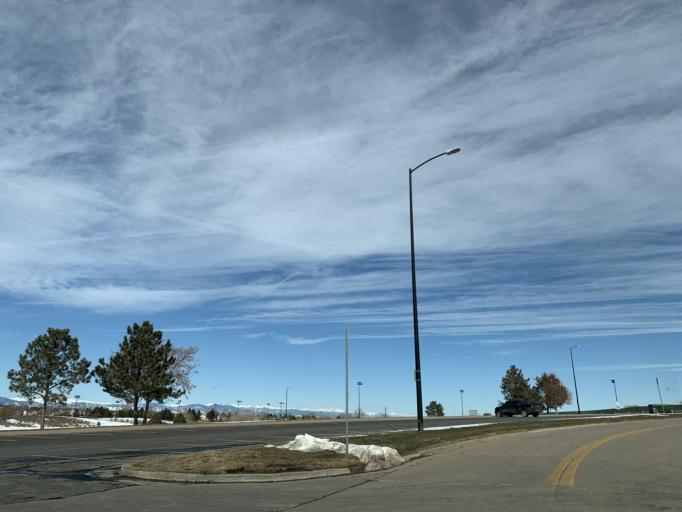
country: US
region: Colorado
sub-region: Douglas County
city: Carriage Club
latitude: 39.5404
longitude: -104.9170
